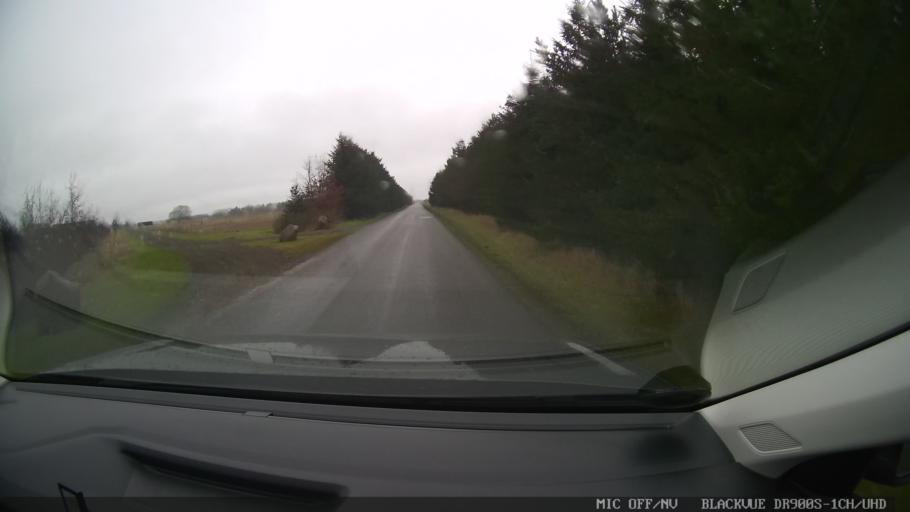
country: DK
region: Central Jutland
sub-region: Viborg Kommune
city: Karup
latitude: 56.2419
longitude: 9.1423
